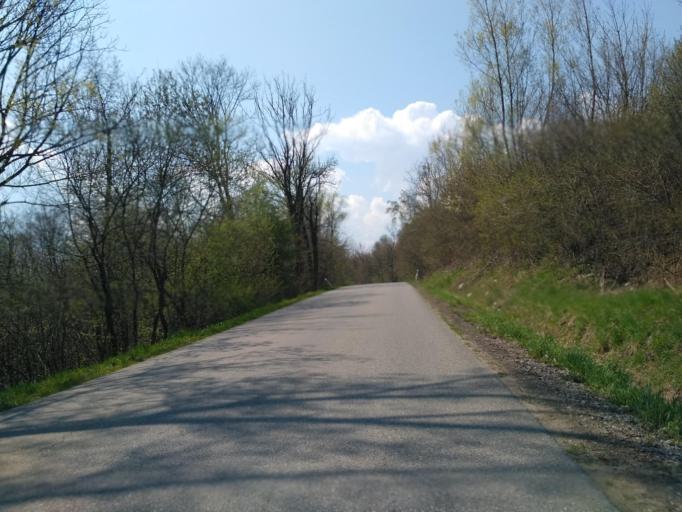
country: PL
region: Subcarpathian Voivodeship
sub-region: Powiat sanocki
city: Zarszyn
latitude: 49.5547
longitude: 21.9907
